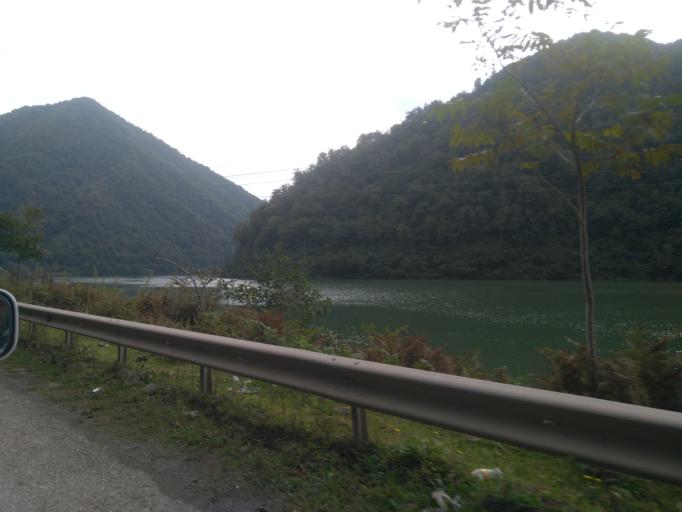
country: GE
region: Ajaria
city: Khelvachauri
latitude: 41.5455
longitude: 41.7123
